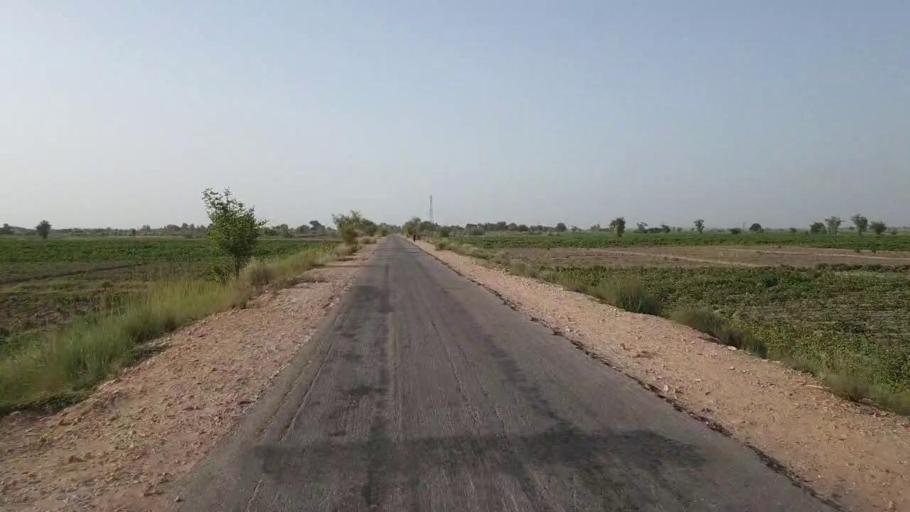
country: PK
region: Sindh
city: Jam Sahib
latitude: 26.4748
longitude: 68.8598
